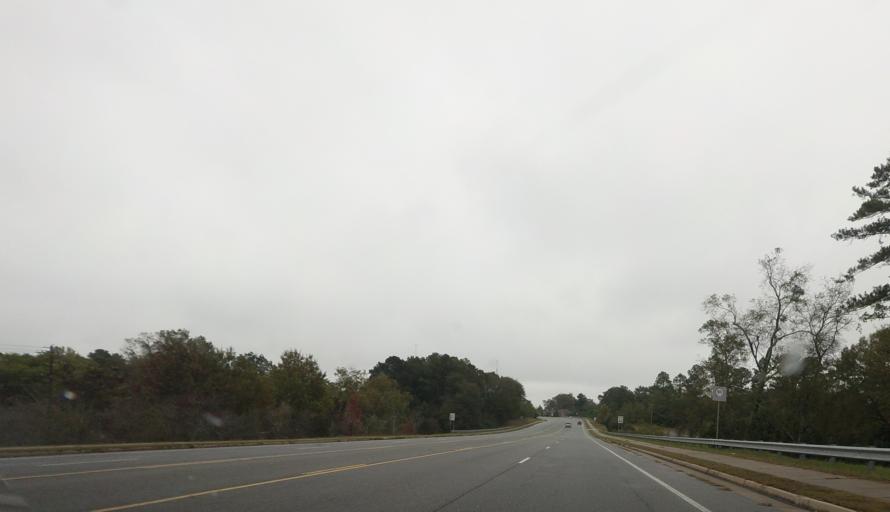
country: US
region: Georgia
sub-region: Taylor County
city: Reynolds
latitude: 32.5595
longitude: -84.1035
